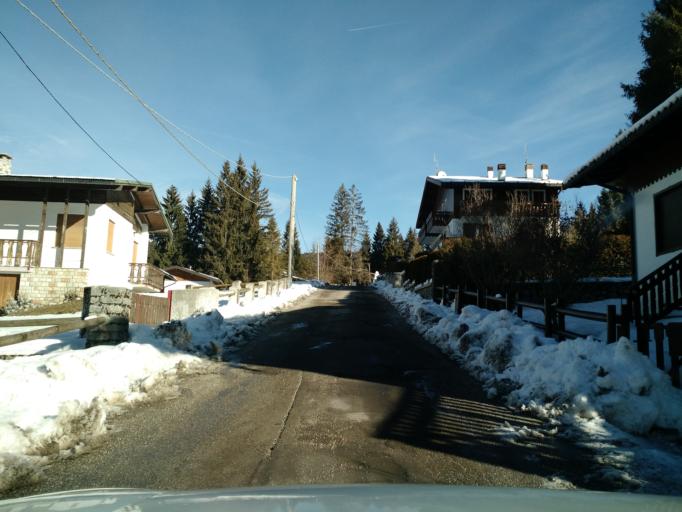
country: IT
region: Veneto
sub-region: Provincia di Vicenza
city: Gallio
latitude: 45.8858
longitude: 11.5342
